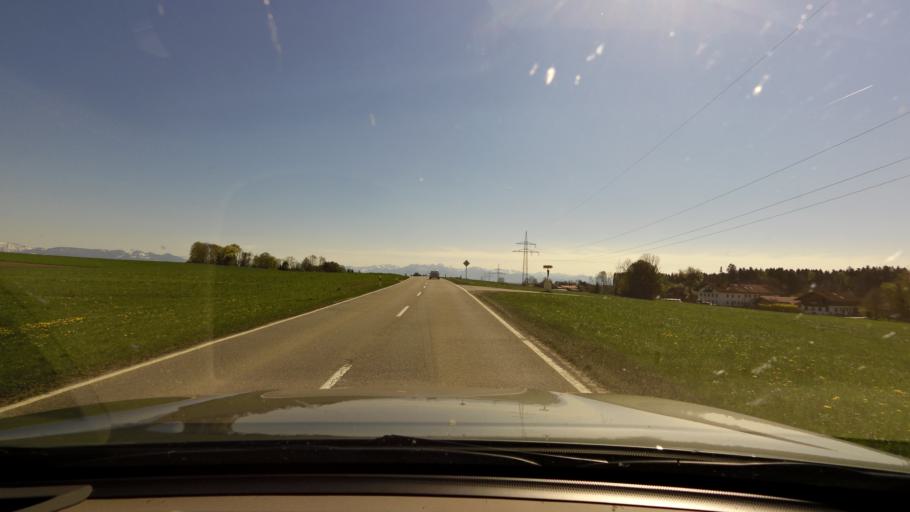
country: DE
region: Bavaria
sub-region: Upper Bavaria
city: Griesstatt
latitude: 47.9747
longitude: 12.1763
